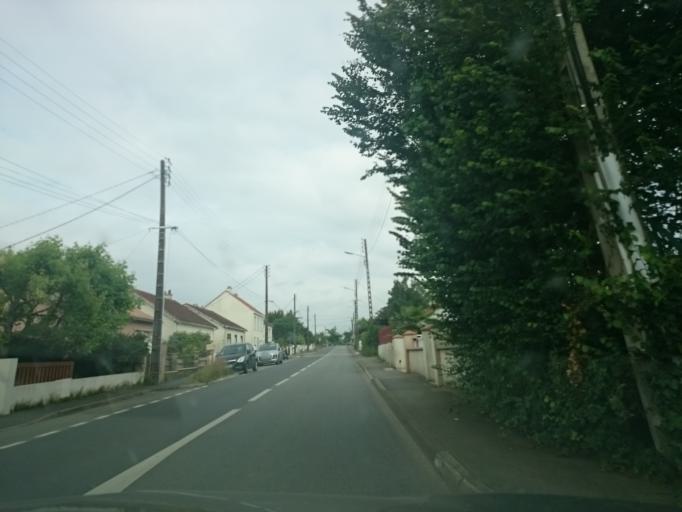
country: FR
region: Pays de la Loire
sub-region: Departement de la Loire-Atlantique
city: Saint-Jean-de-Boiseau
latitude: 47.1930
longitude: -1.7181
